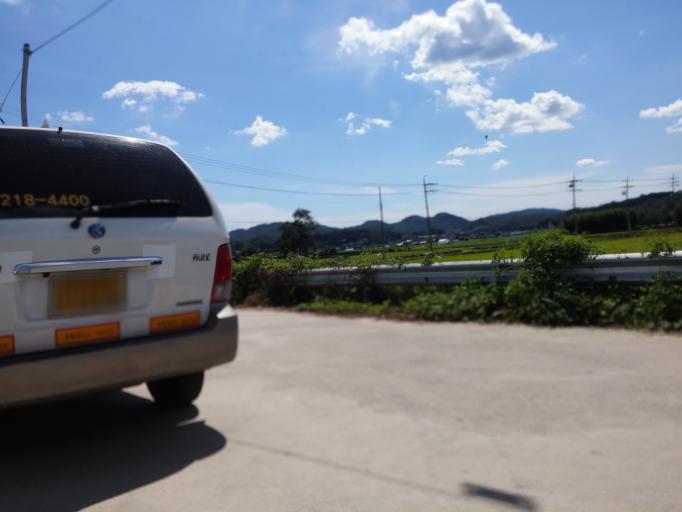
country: KR
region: Chungcheongbuk-do
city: Cheongju-si
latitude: 36.5956
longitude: 127.4970
